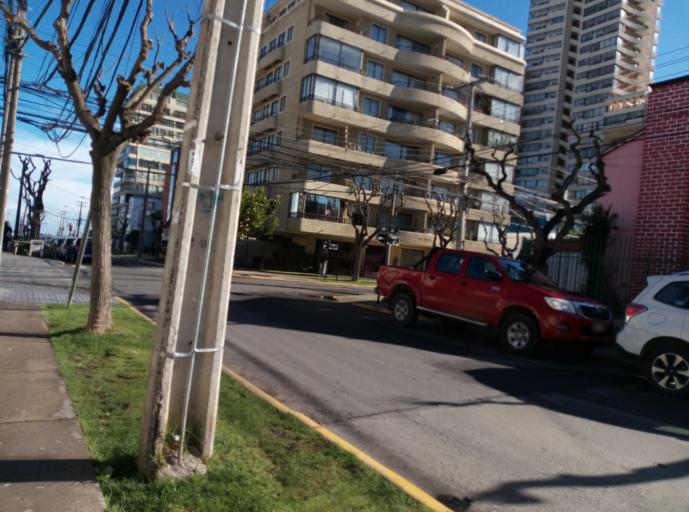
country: CL
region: Valparaiso
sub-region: Provincia de Valparaiso
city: Vina del Mar
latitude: -33.0090
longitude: -71.5498
